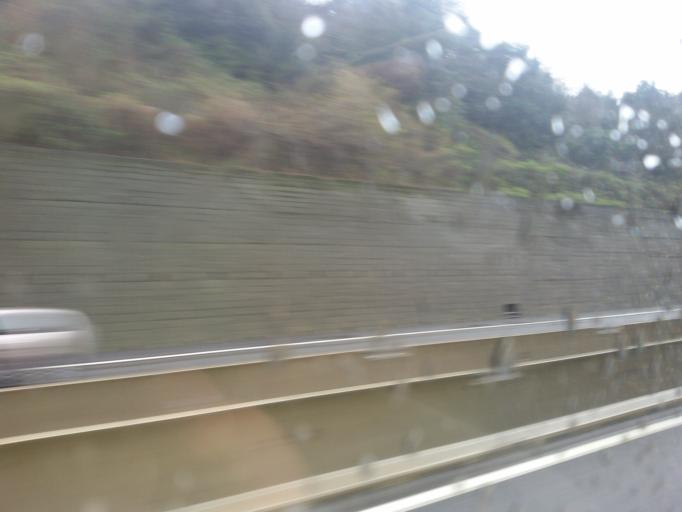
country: IT
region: Tuscany
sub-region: Province of Arezzo
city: Viciomaggio
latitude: 43.4552
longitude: 11.7544
